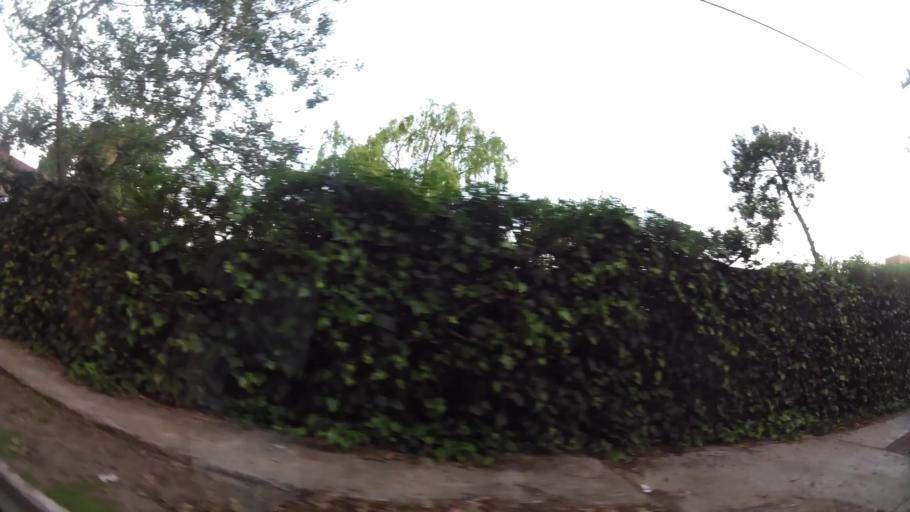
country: AR
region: Buenos Aires
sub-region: Partido de Quilmes
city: Quilmes
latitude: -34.7781
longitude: -58.2134
